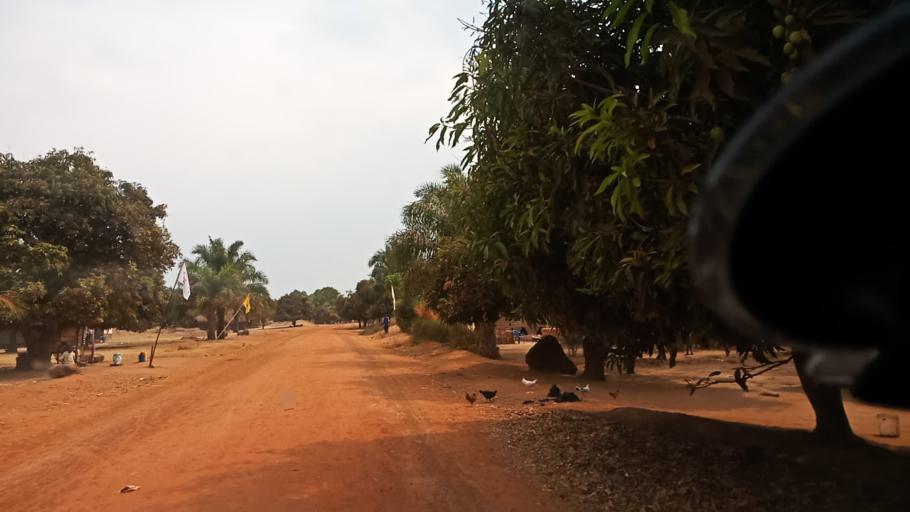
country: ZM
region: Luapula
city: Nchelenge
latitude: -9.1327
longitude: 28.2990
